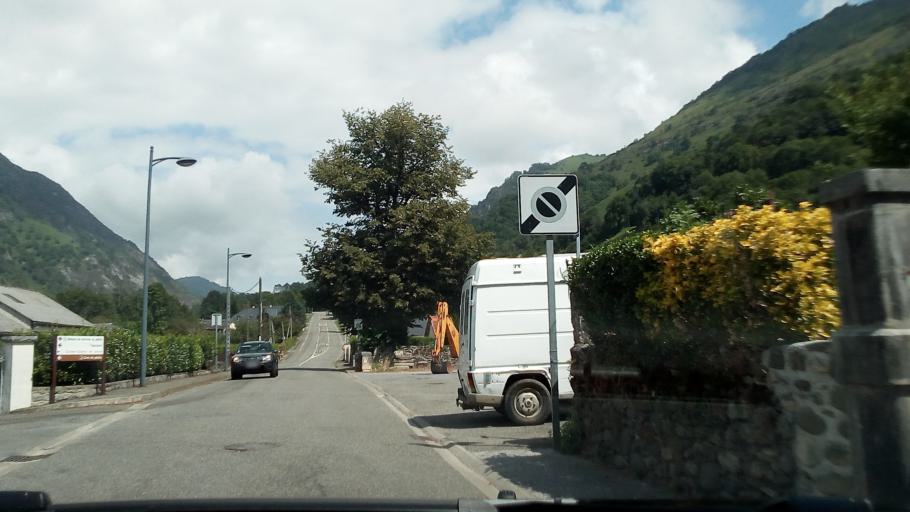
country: FR
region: Aquitaine
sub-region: Departement des Pyrenees-Atlantiques
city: Arette
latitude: 43.0008
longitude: -0.6011
